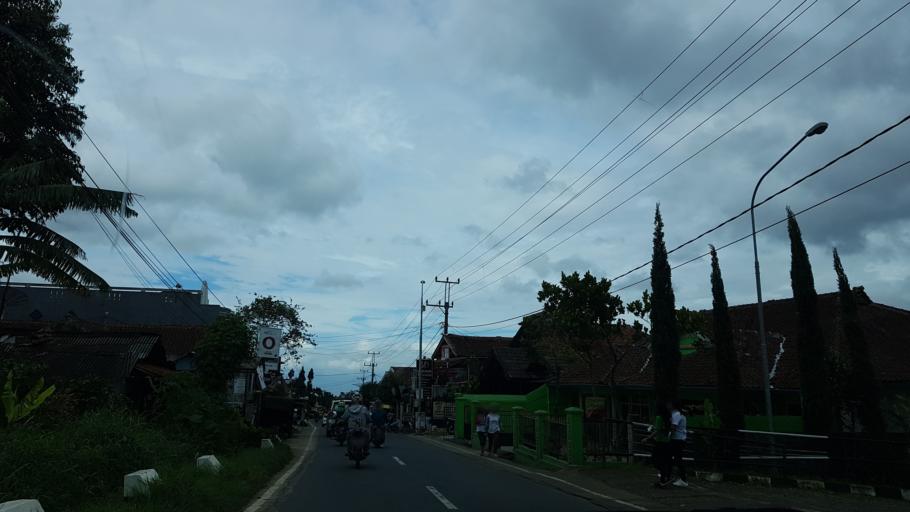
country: ID
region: West Java
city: Banjar
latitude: -7.1148
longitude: 107.4377
